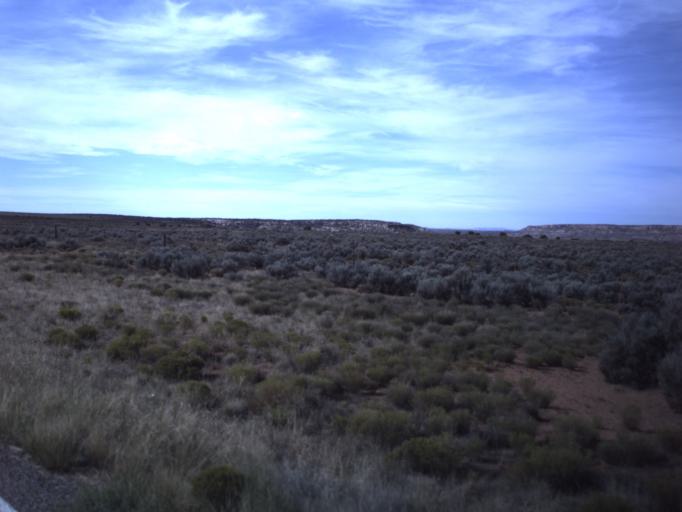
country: US
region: Utah
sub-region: San Juan County
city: Blanding
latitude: 37.3725
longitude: -109.3430
